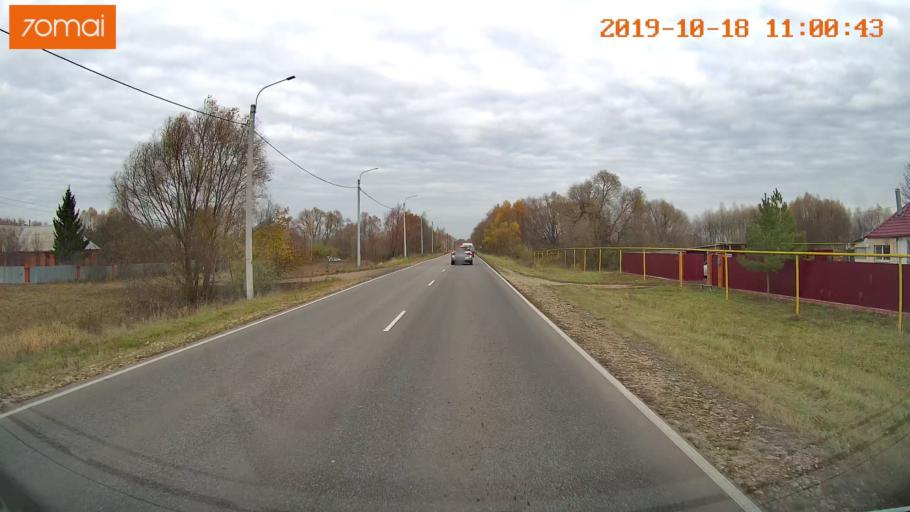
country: RU
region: Tula
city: Yepifan'
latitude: 53.8464
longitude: 38.5527
